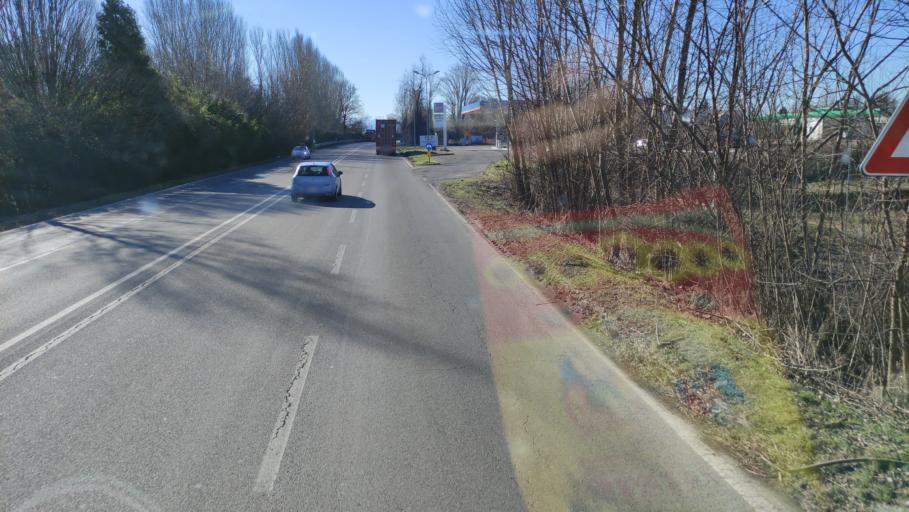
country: IT
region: Emilia-Romagna
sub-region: Provincia di Reggio Emilia
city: Correggio
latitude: 44.7627
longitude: 10.8100
